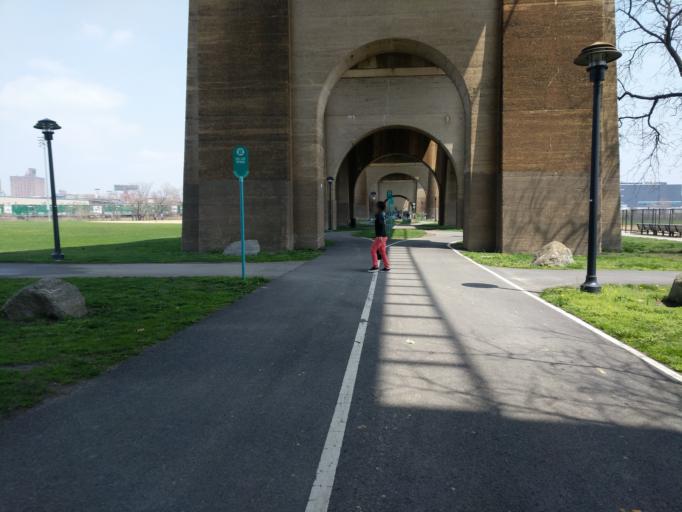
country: US
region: New York
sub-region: New York County
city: Manhattan
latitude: 40.7968
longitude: -73.9179
